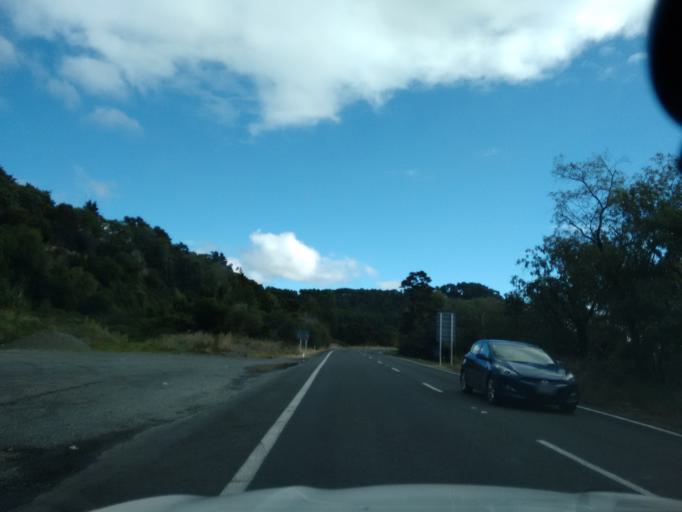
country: NZ
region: Waikato
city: Turangi
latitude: -38.8856
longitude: 175.9644
